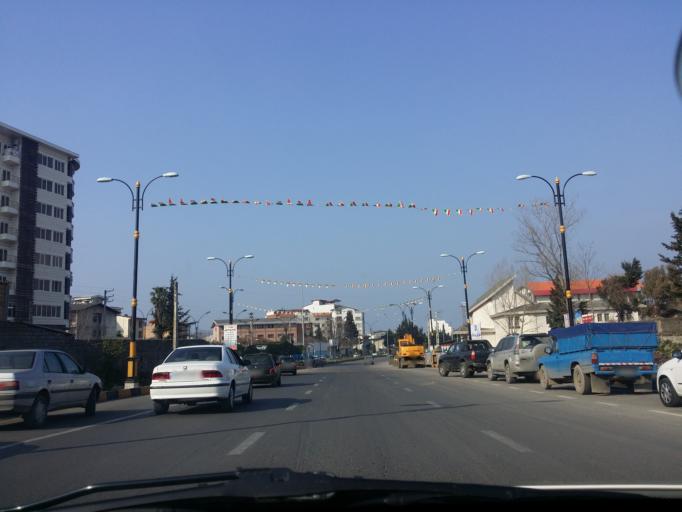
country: IR
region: Mazandaran
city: Chalus
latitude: 36.6571
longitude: 51.4224
